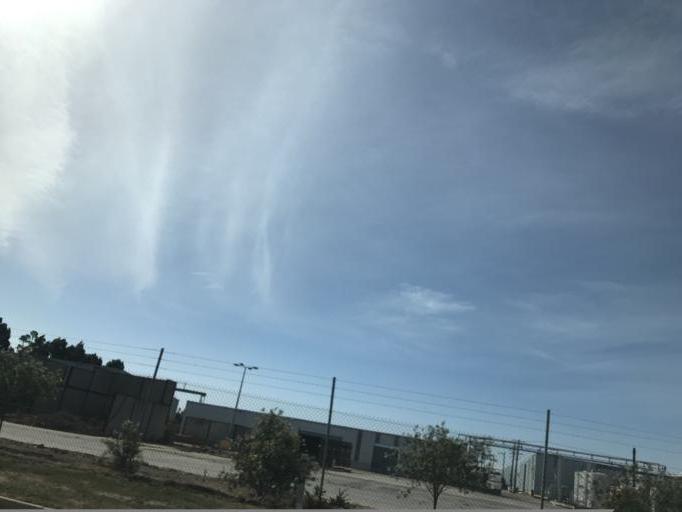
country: AU
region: Victoria
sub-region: Ballarat North
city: Newington
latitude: -37.5345
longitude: 143.8089
